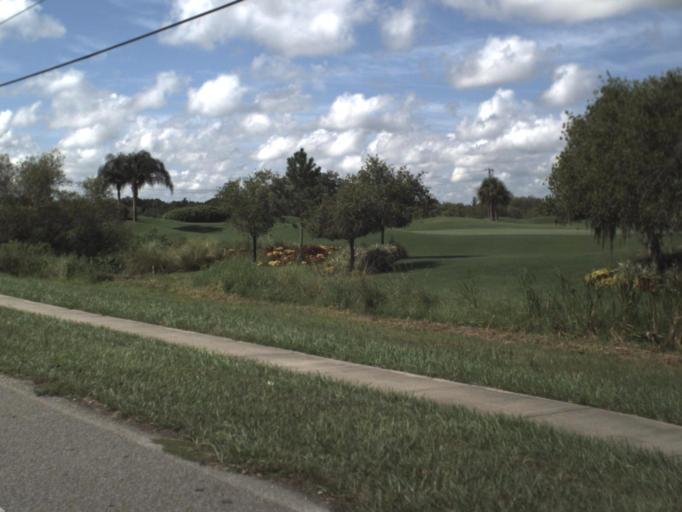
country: US
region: Florida
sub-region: Polk County
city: Lakeland
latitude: 28.0086
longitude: -81.9752
